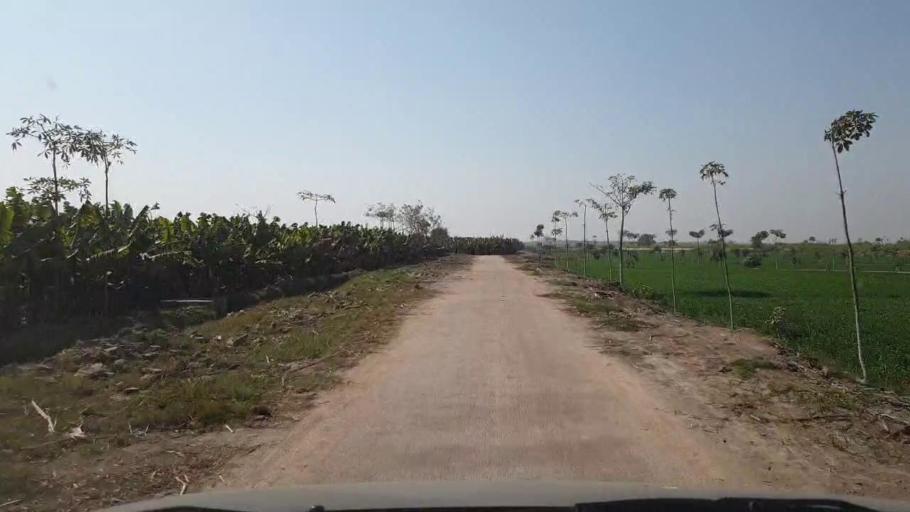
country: PK
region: Sindh
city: Tando Jam
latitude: 25.4103
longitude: 68.6238
